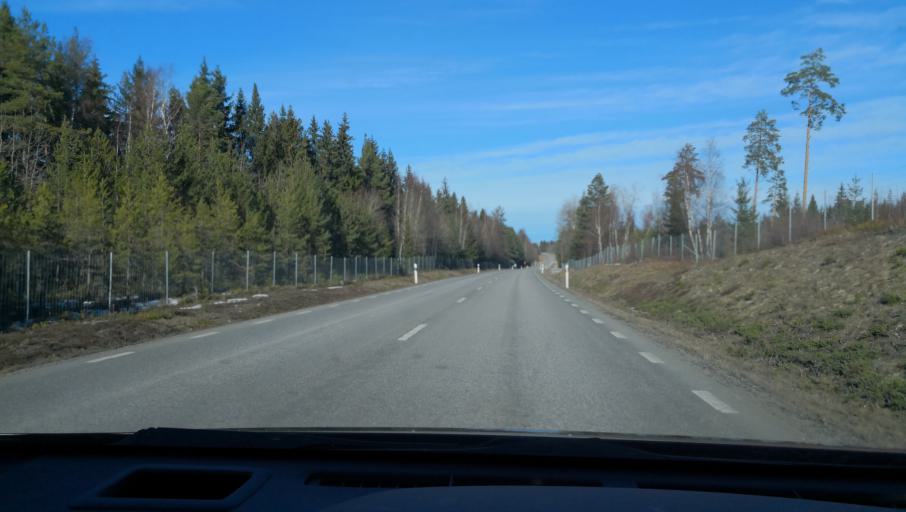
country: SE
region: Uppsala
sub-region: Uppsala Kommun
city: Vattholma
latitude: 60.0531
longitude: 17.7520
